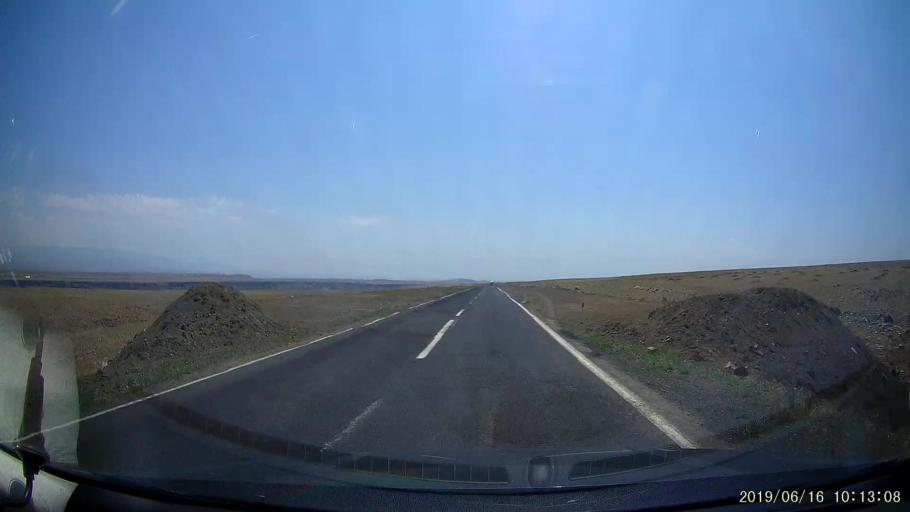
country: TR
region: Igdir
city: Tuzluca
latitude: 40.1937
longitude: 43.6363
